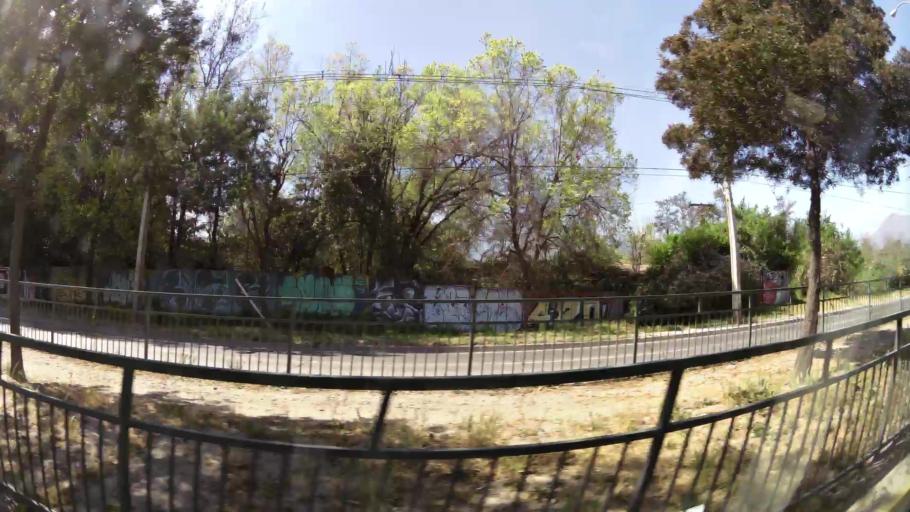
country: CL
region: Santiago Metropolitan
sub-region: Provincia de Cordillera
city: Puente Alto
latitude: -33.5826
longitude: -70.5482
